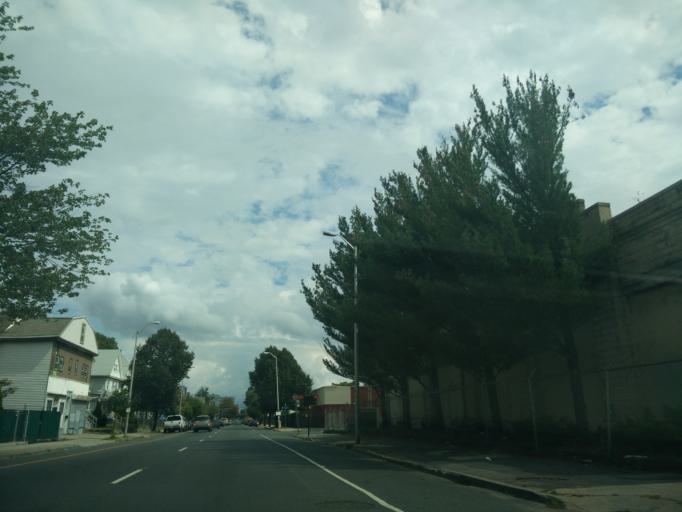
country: US
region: Connecticut
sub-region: Fairfield County
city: Bridgeport
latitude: 41.1715
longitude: -73.2054
